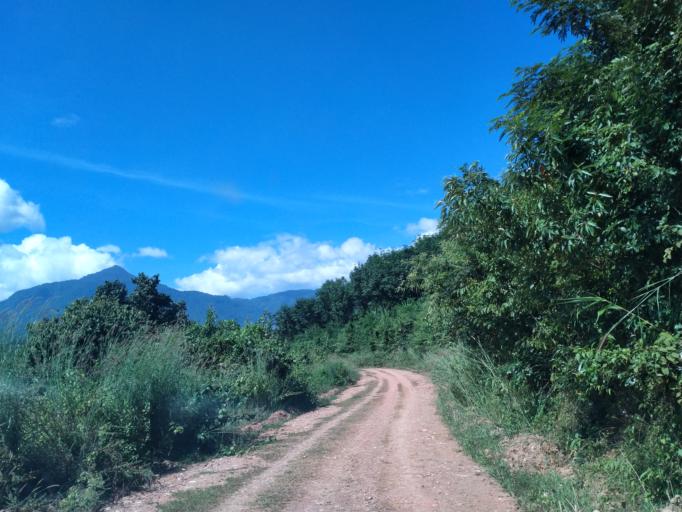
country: LA
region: Vientiane
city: Muang Phon-Hong
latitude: 18.6198
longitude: 102.8631
